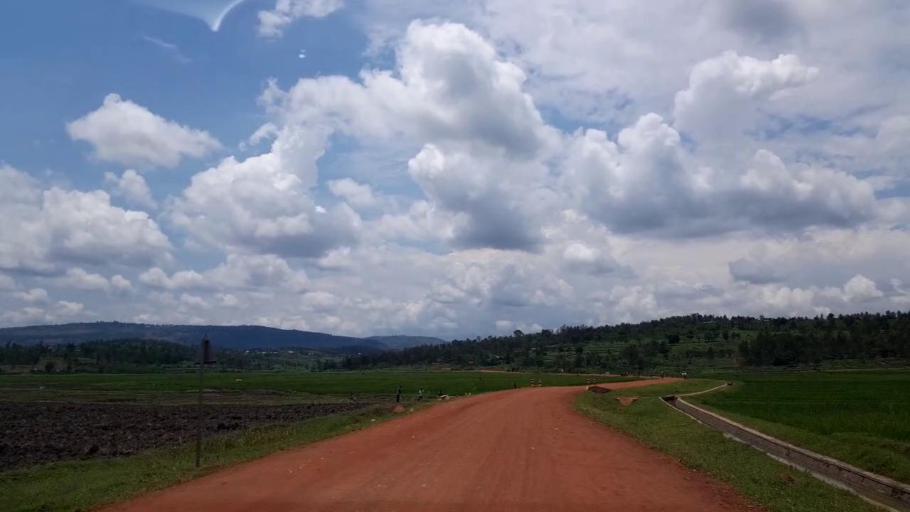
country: RW
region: Northern Province
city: Byumba
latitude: -1.5704
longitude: 30.2927
